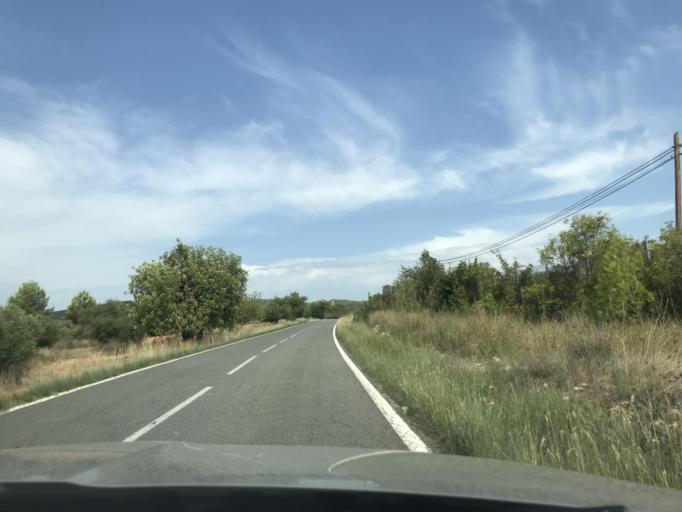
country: ES
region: Catalonia
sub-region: Provincia de Tarragona
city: Altafulla
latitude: 41.1742
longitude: 1.3722
